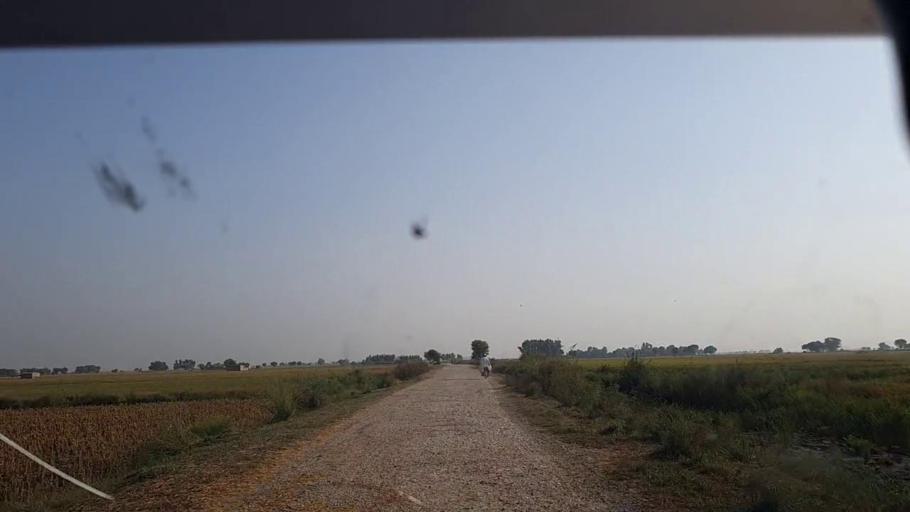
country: PK
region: Sindh
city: Shikarpur
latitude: 28.0683
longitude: 68.5462
